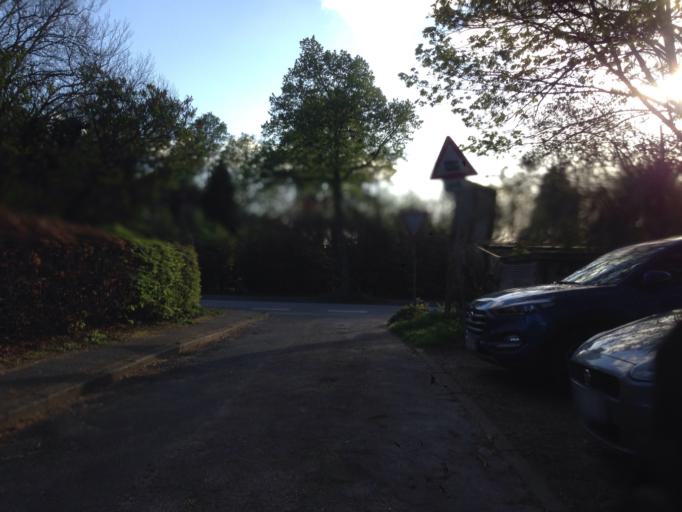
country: DE
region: Hamburg
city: Marienthal
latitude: 53.5677
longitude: 10.0694
